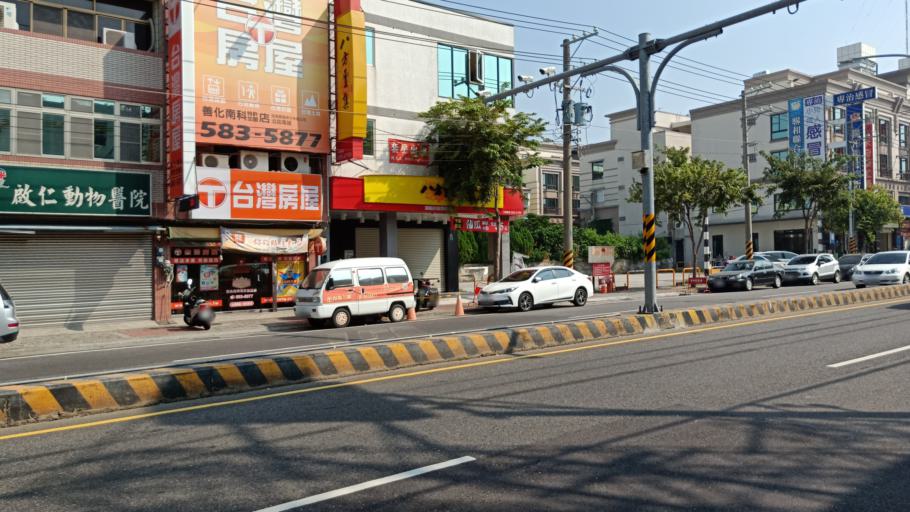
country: TW
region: Taiwan
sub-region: Tainan
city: Tainan
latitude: 23.1295
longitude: 120.2975
